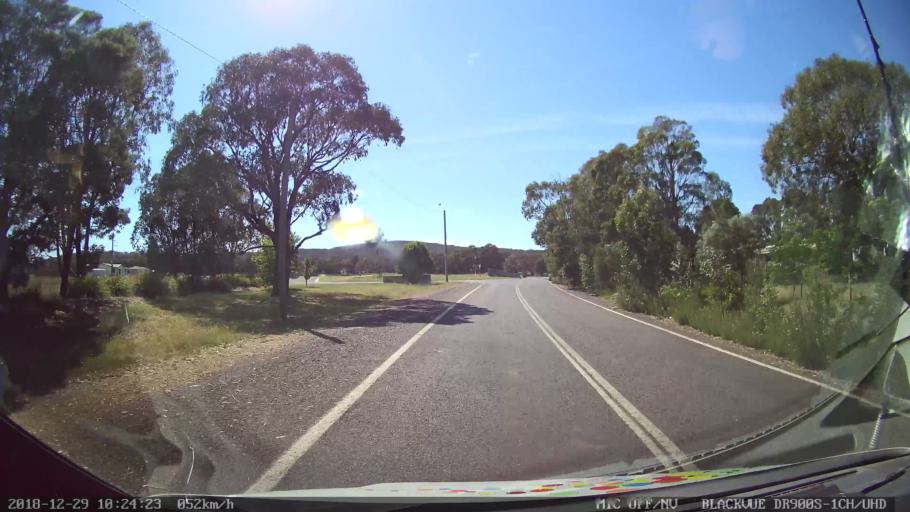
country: AU
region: New South Wales
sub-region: Yass Valley
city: Gundaroo
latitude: -34.9130
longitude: 149.4379
